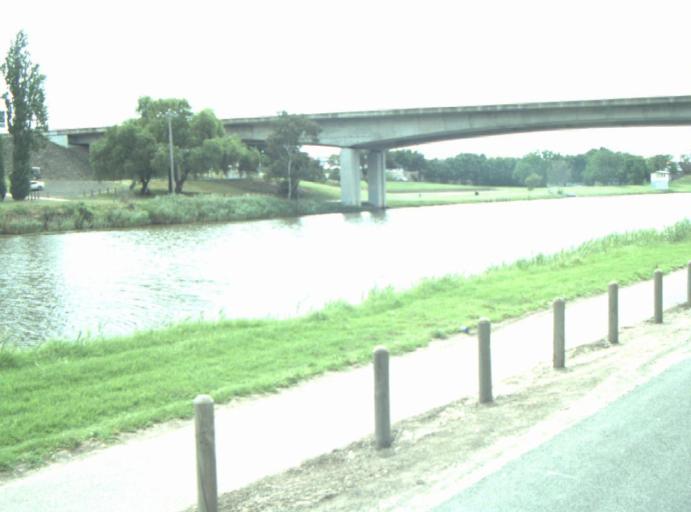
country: AU
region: Victoria
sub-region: Greater Geelong
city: Geelong
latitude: -38.1646
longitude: 144.3485
